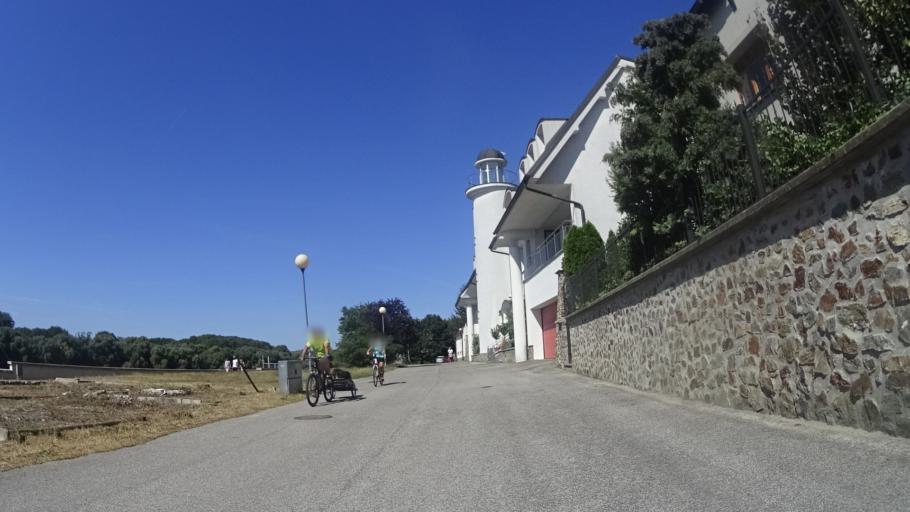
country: AT
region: Lower Austria
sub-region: Politischer Bezirk Bruck an der Leitha
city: Wolfsthal
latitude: 48.1712
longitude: 16.9817
